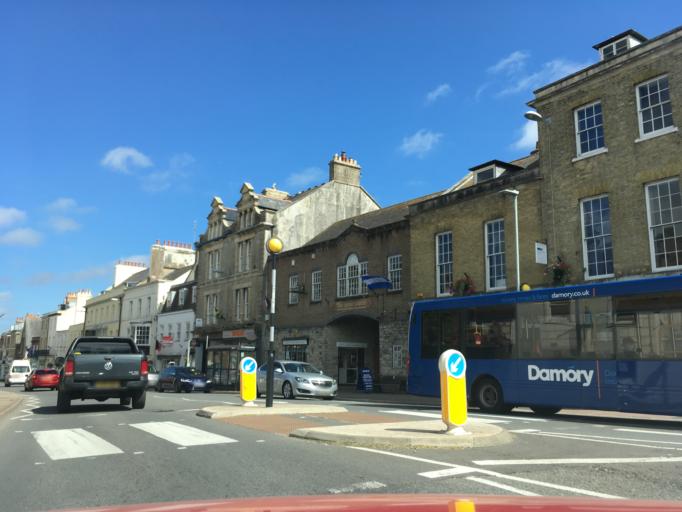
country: GB
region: England
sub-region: Dorset
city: Dorchester
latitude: 50.7150
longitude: -2.4415
